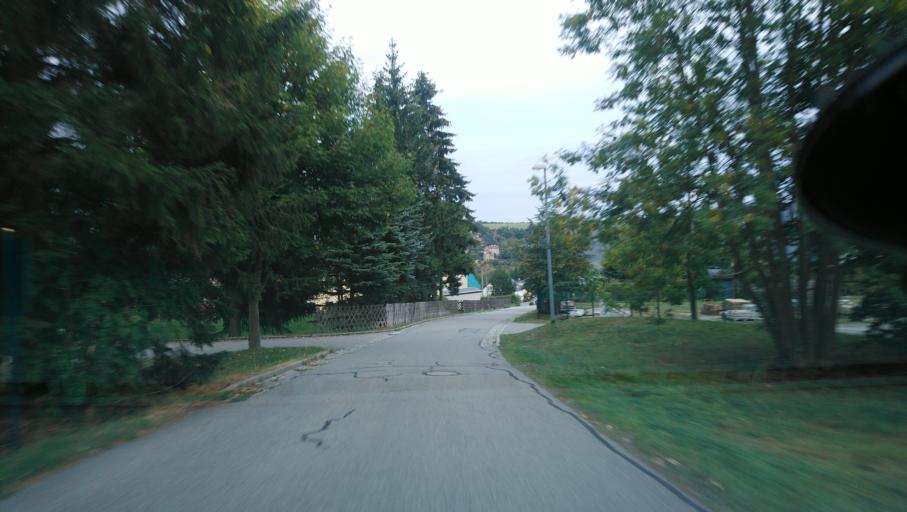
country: DE
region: Saxony
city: Barenstein
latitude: 50.5025
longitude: 13.0254
